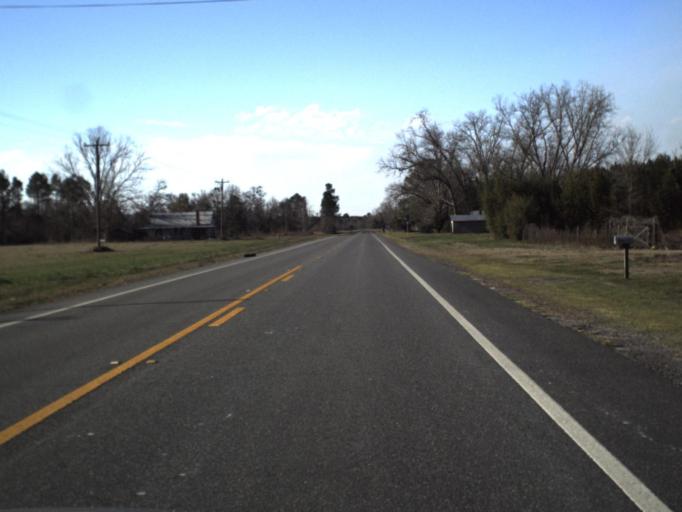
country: US
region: Florida
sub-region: Calhoun County
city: Blountstown
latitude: 30.4628
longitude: -85.1943
